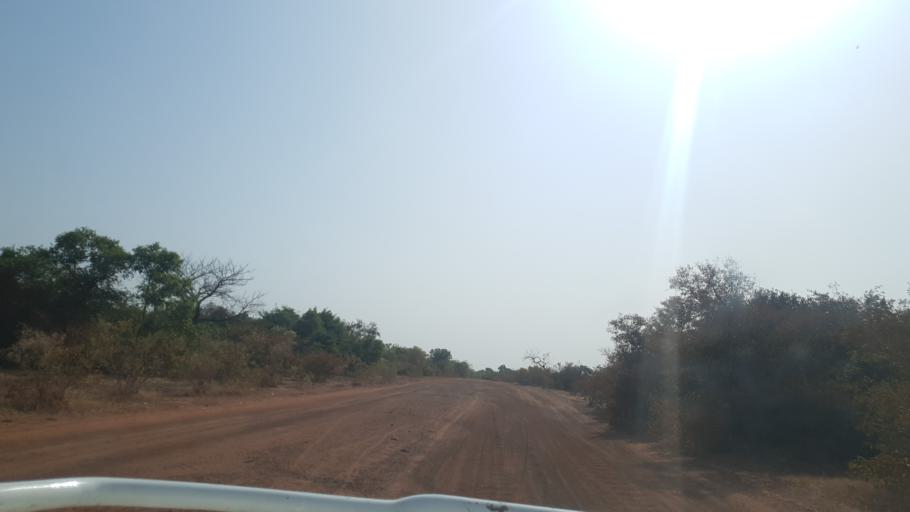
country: ML
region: Koulikoro
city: Dioila
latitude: 12.6717
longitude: -6.7063
